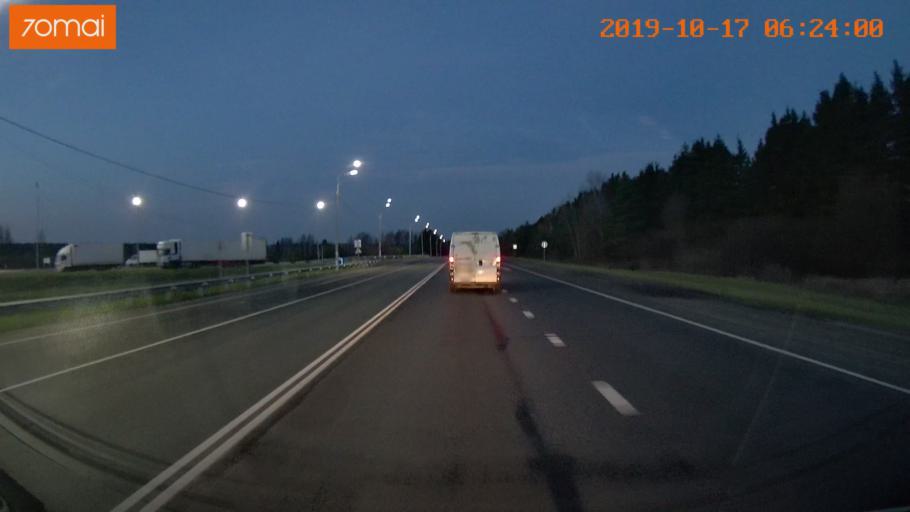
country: RU
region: Ivanovo
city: Lezhnevo
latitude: 56.7791
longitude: 40.8371
